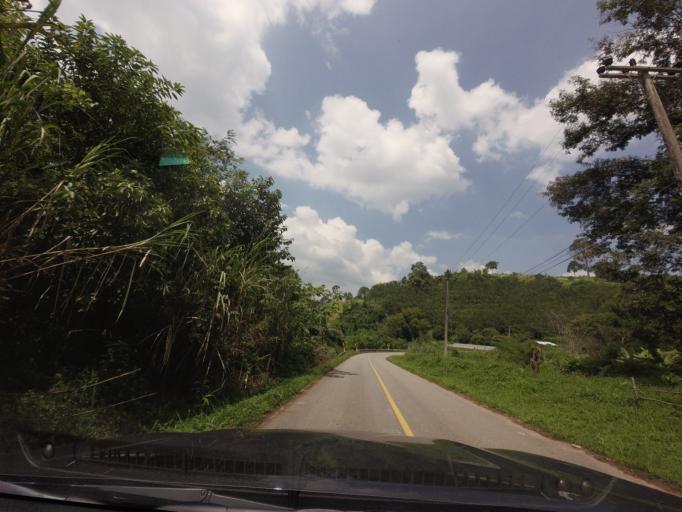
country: TH
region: Loei
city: Na Haeo
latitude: 17.6646
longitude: 100.9229
